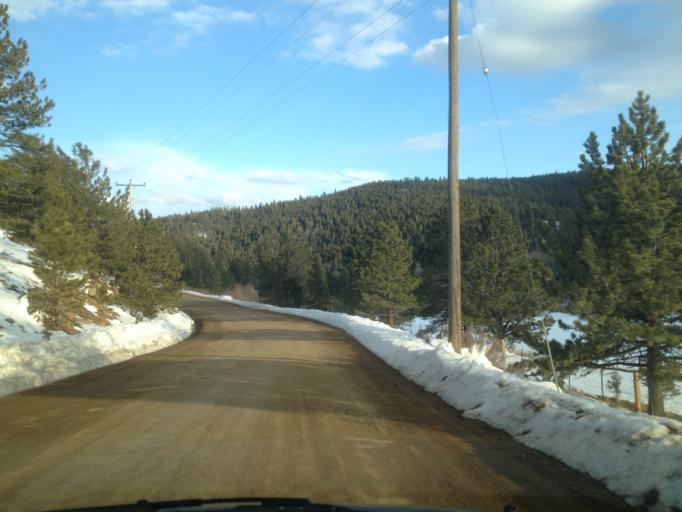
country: US
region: Colorado
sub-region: Boulder County
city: Nederland
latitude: 40.1229
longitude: -105.4531
